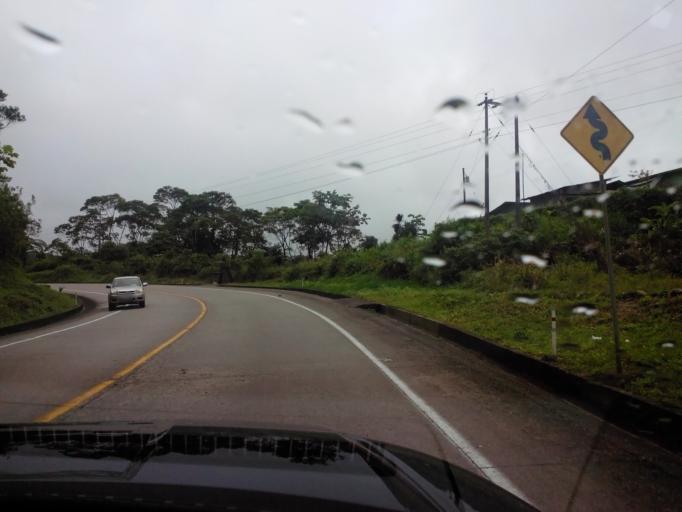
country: EC
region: Napo
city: Archidona
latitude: -0.7888
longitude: -77.7798
